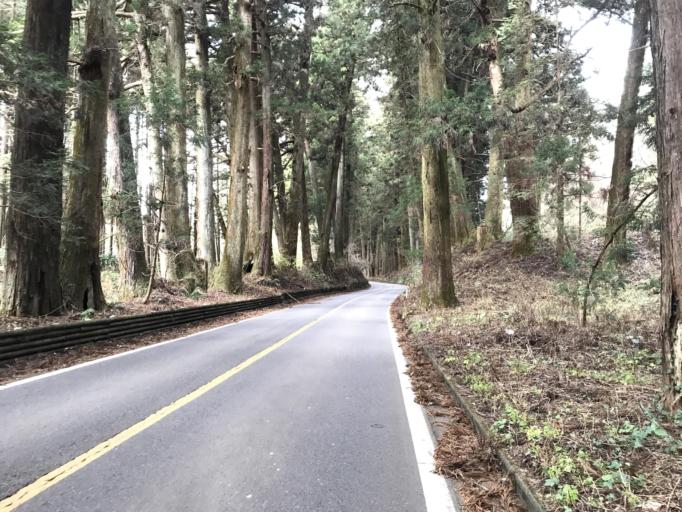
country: JP
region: Tochigi
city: Imaichi
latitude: 36.6949
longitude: 139.7133
